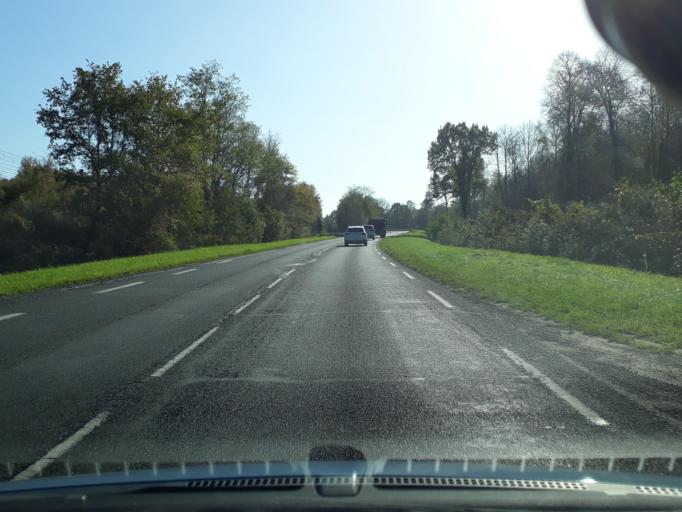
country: FR
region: Ile-de-France
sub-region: Departement de Seine-et-Marne
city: Livry-sur-Seine
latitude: 48.5046
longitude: 2.6829
